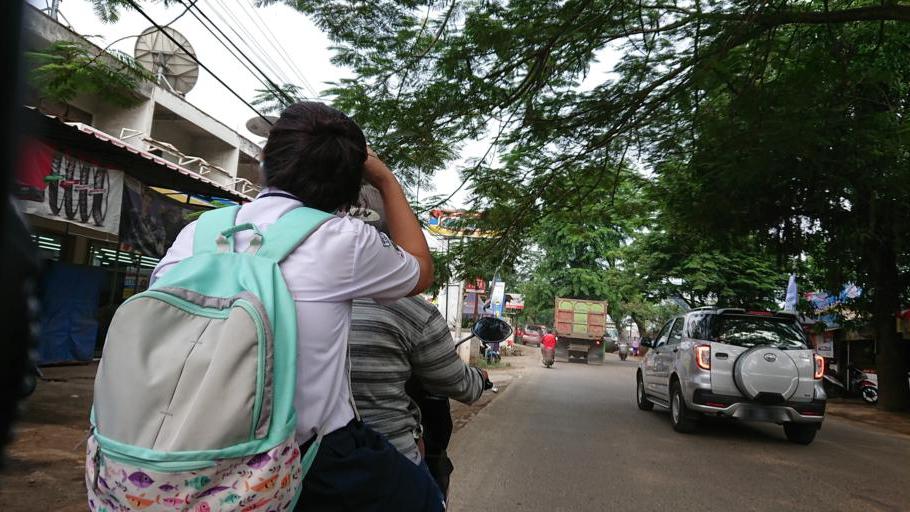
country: ID
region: West Java
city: Parung
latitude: -6.3841
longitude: 106.6826
